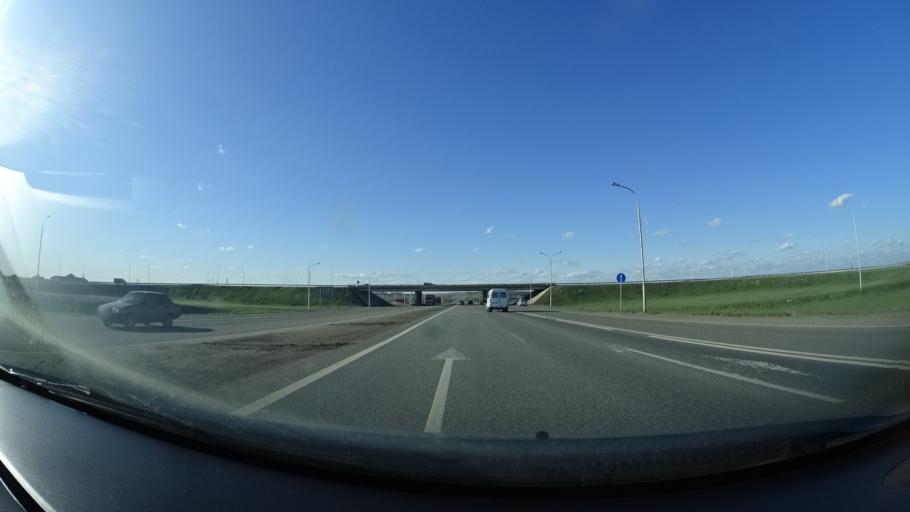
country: RU
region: Bashkortostan
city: Kabakovo
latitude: 54.4912
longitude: 55.9065
